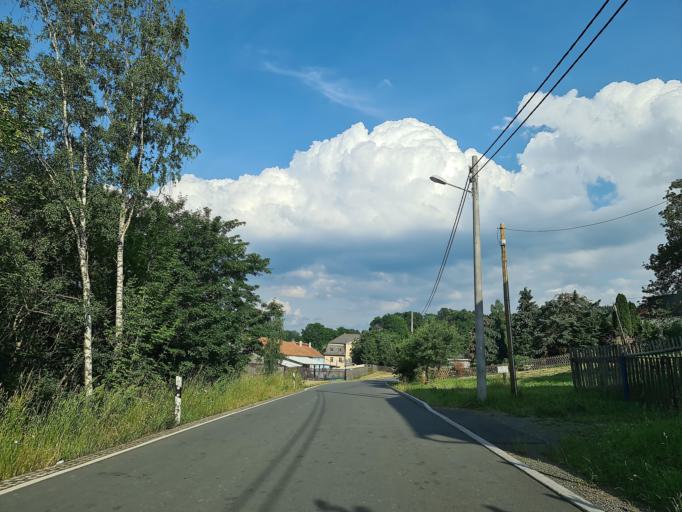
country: DE
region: Saxony
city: Bosenbrunn
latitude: 50.3984
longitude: 12.0977
